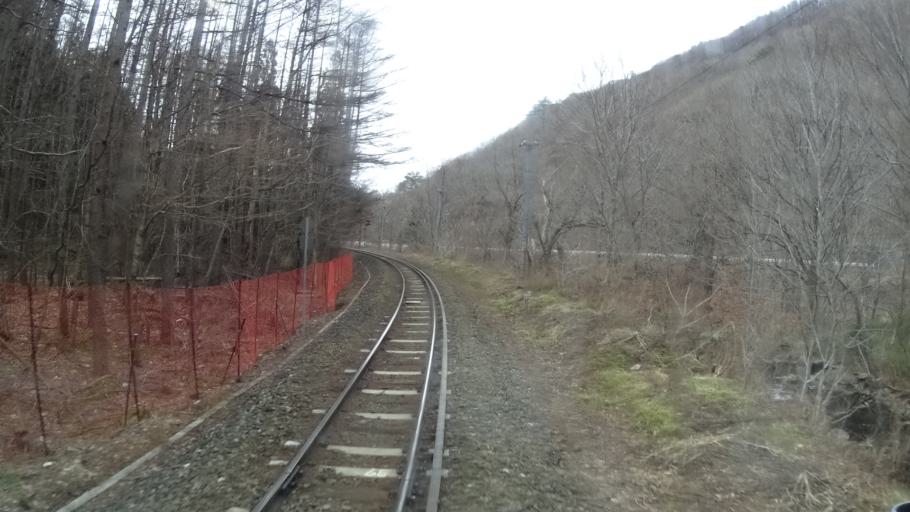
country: JP
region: Iwate
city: Tono
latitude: 39.2567
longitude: 141.6522
